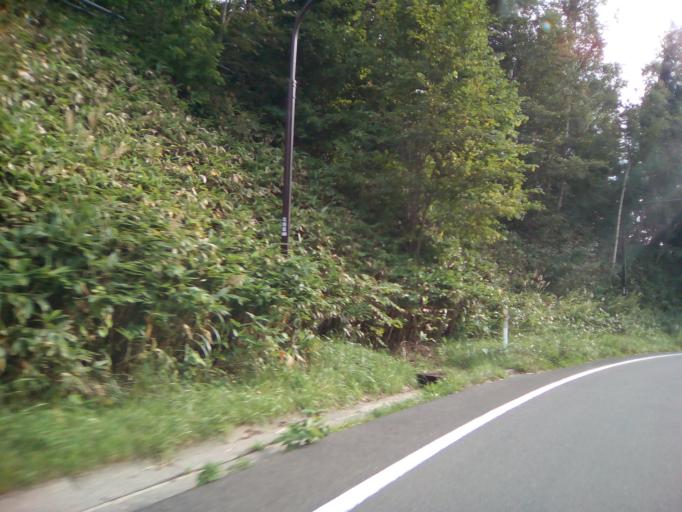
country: JP
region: Hokkaido
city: Date
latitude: 42.6620
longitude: 140.8400
